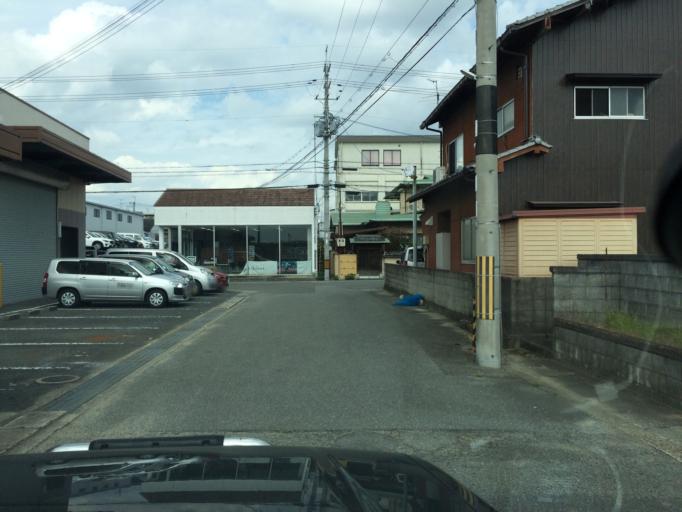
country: JP
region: Kyoto
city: Tanabe
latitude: 34.8186
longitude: 135.7848
